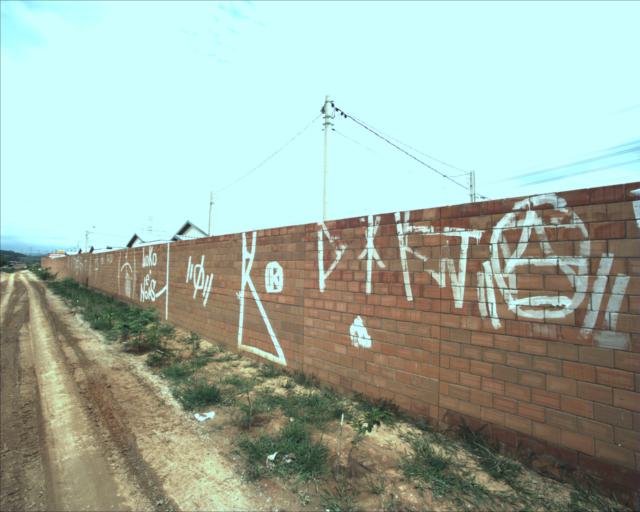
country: BR
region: Sao Paulo
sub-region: Sorocaba
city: Sorocaba
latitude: -23.4533
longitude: -47.3843
